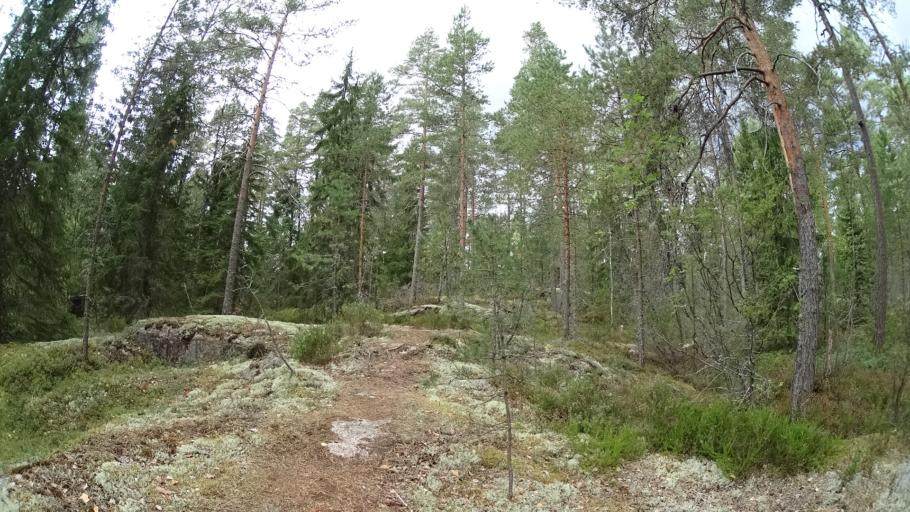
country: FI
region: Uusimaa
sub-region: Helsinki
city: Espoo
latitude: 60.3017
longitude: 24.5842
